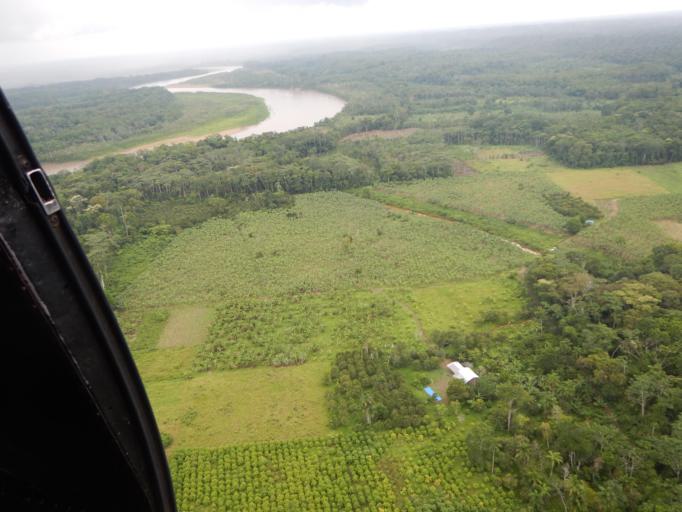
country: BO
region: Cochabamba
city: Chimore
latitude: -17.0794
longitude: -64.7783
